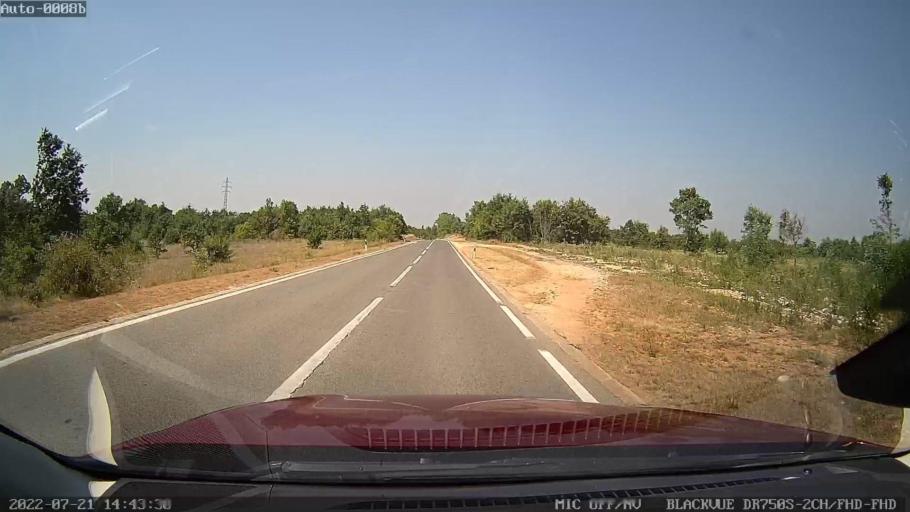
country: HR
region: Istarska
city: Pazin
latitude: 45.1095
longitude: 13.8834
